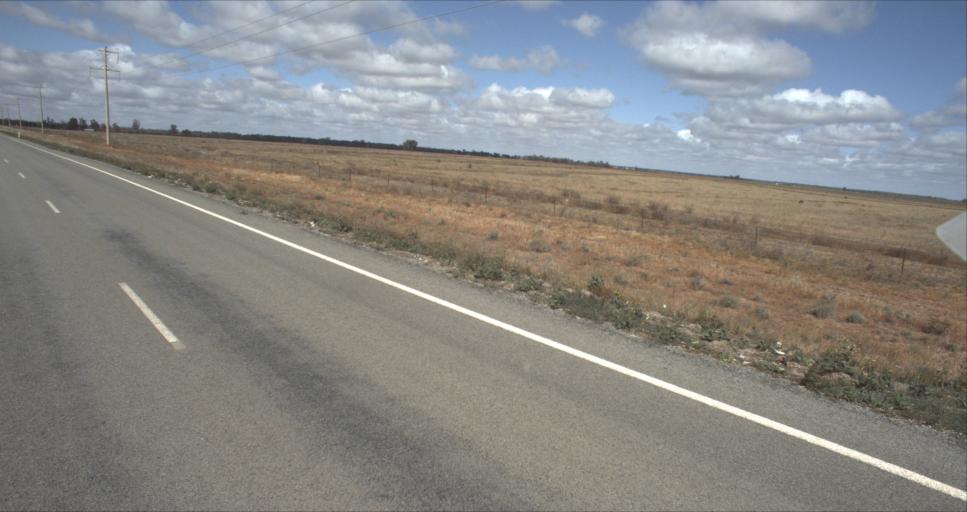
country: AU
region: New South Wales
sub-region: Murrumbidgee Shire
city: Darlington Point
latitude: -34.5808
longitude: 146.1651
